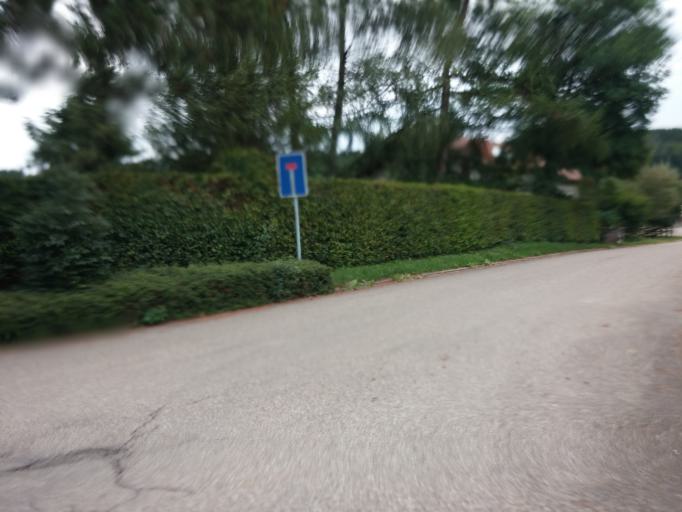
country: DE
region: Bavaria
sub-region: Swabia
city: Lautrach
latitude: 47.9017
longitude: 10.1316
